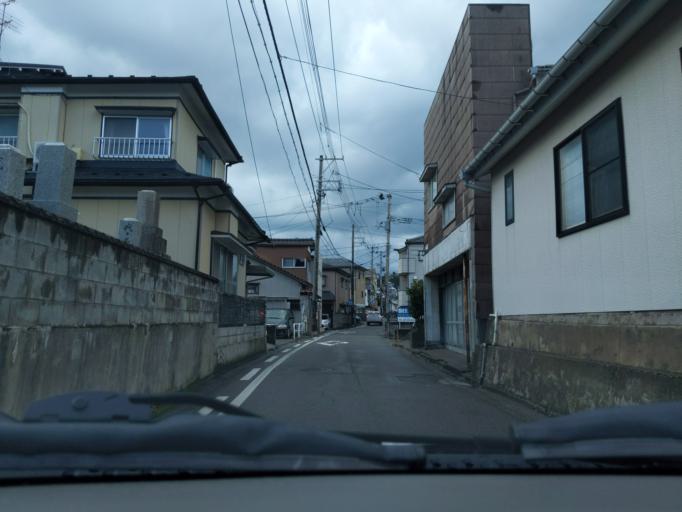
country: JP
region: Niigata
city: Niigata-shi
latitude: 37.9292
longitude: 139.0443
